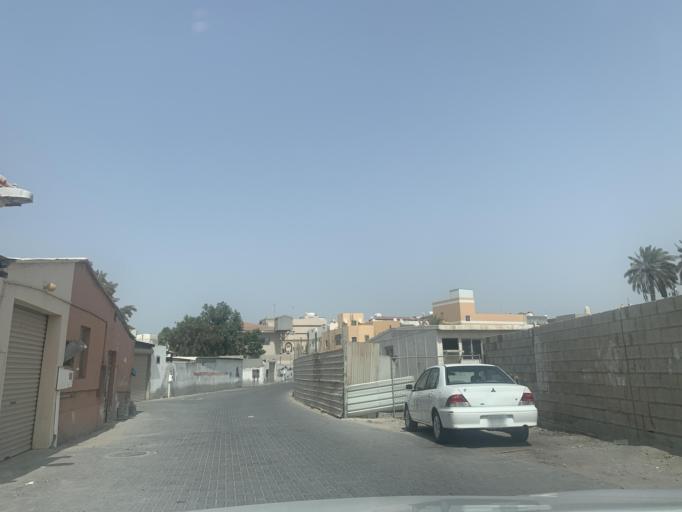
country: BH
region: Manama
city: Jidd Hafs
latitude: 26.2189
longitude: 50.4690
